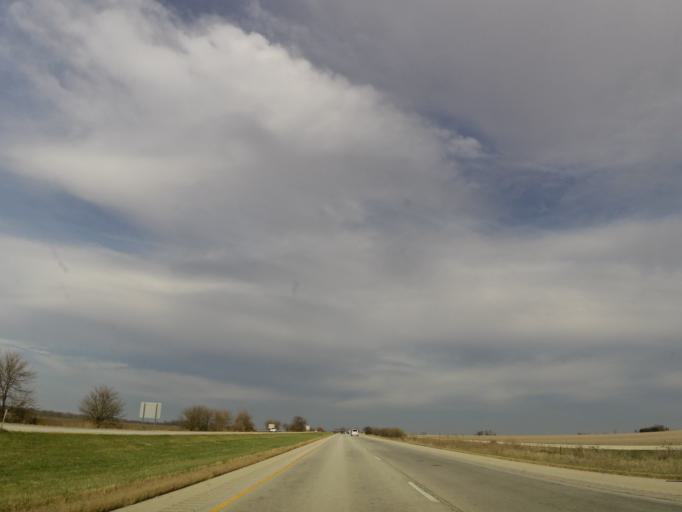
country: US
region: Illinois
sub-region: Knox County
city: Galesburg
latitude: 40.9961
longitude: -90.3356
